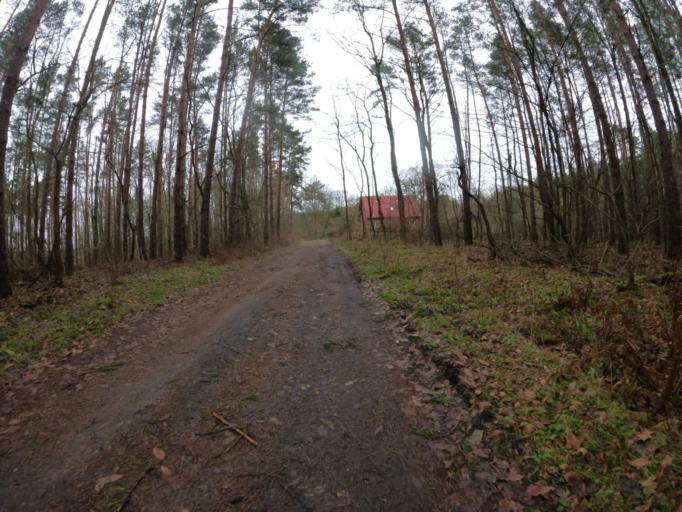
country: PL
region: West Pomeranian Voivodeship
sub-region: Powiat mysliborski
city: Debno
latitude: 52.7405
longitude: 14.7682
